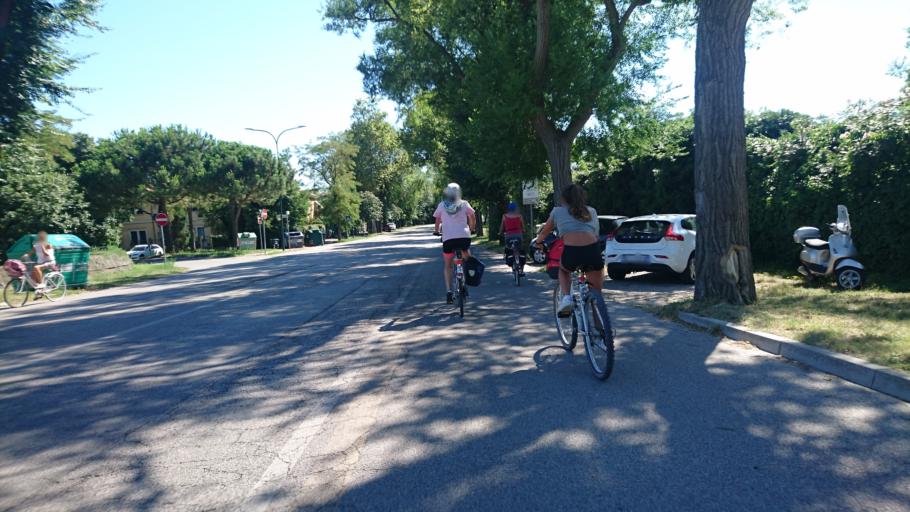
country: IT
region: Veneto
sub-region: Provincia di Venezia
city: Lido
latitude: 45.3750
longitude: 12.3392
